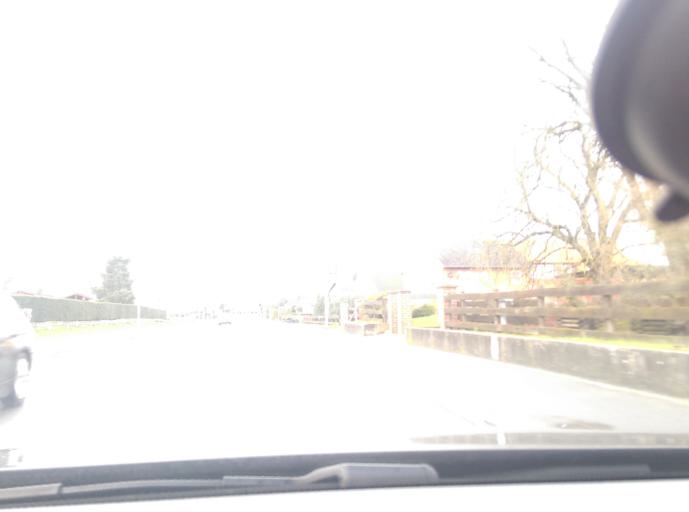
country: DE
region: Lower Saxony
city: Schwarmstedt
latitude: 52.5820
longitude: 9.5885
